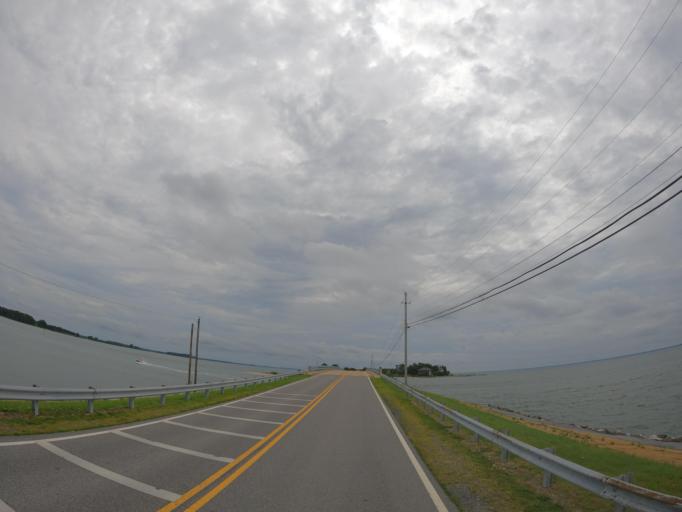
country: US
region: Maryland
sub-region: Saint Mary's County
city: Lexington Park
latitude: 38.1375
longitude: -76.5001
